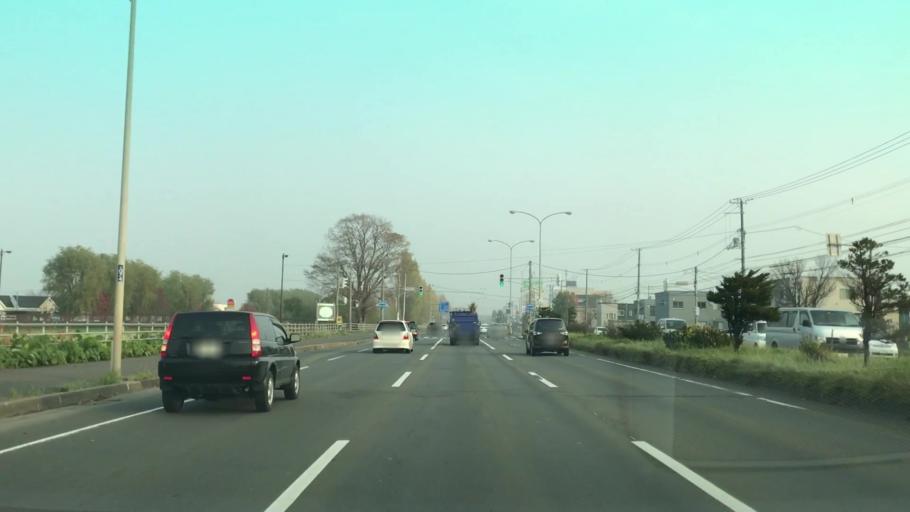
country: JP
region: Hokkaido
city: Ishikari
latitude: 43.1540
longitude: 141.3518
